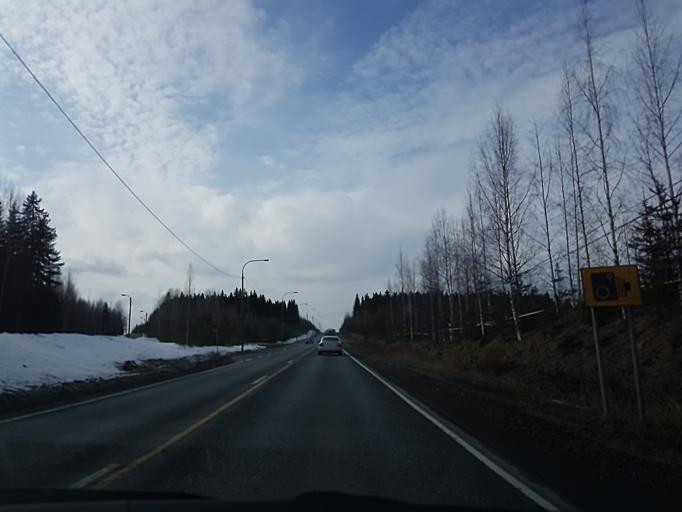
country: FI
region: Northern Savo
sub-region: Kuopio
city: Vehmersalmi
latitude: 62.9414
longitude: 27.9052
